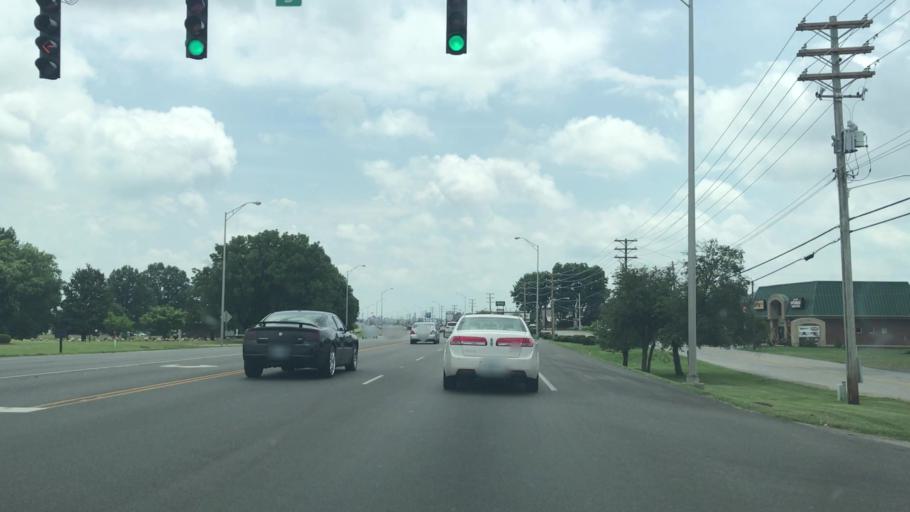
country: US
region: Kentucky
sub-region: Warren County
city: Bowling Green
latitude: 36.9641
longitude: -86.4315
